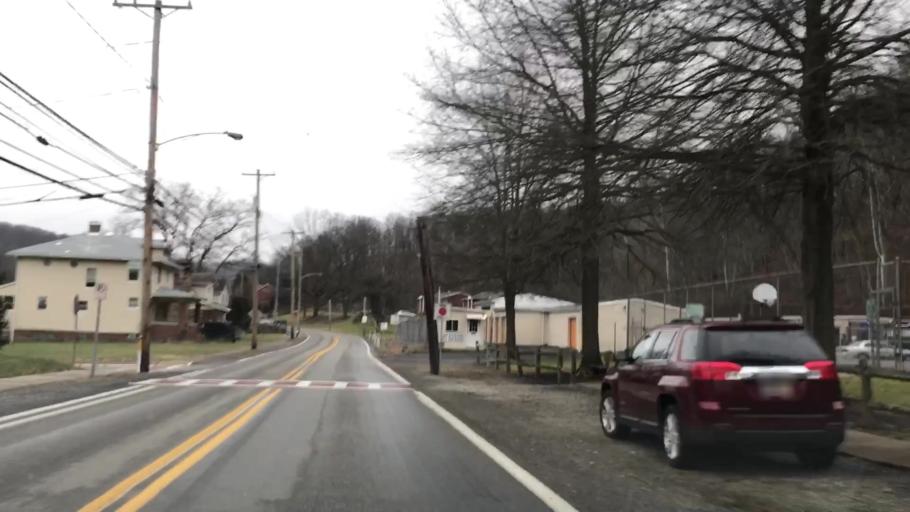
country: US
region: Pennsylvania
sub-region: Beaver County
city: Ambridge
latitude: 40.5835
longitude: -80.2096
